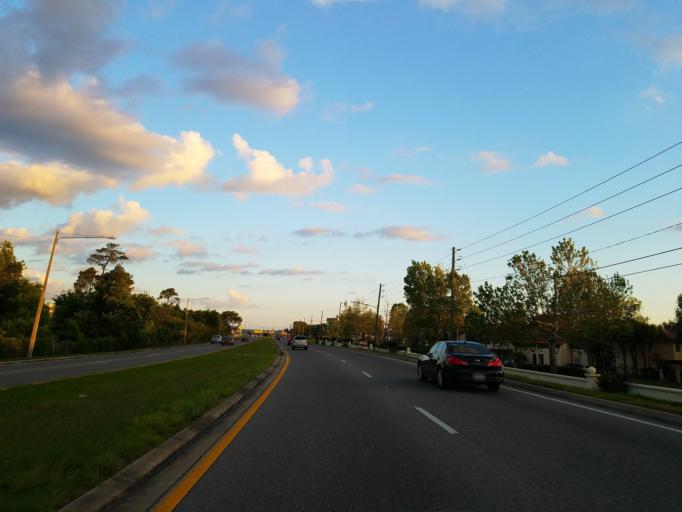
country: US
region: Florida
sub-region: Orange County
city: Williamsburg
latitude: 28.4198
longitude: -81.4761
